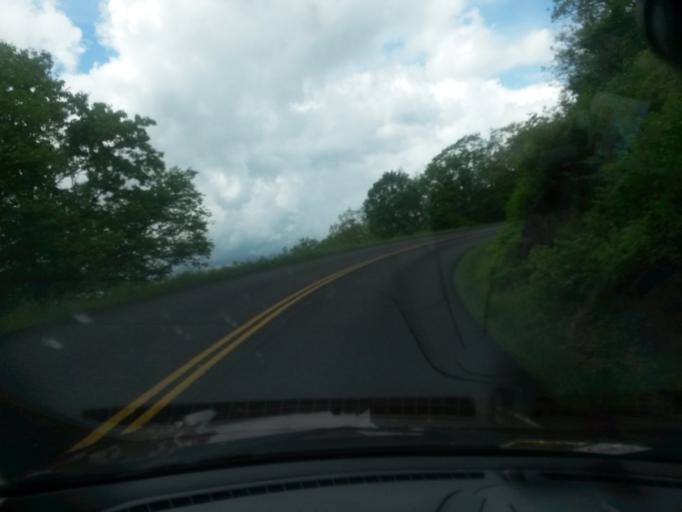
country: US
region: Virginia
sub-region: Floyd County
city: Floyd
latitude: 36.8175
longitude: -80.3457
